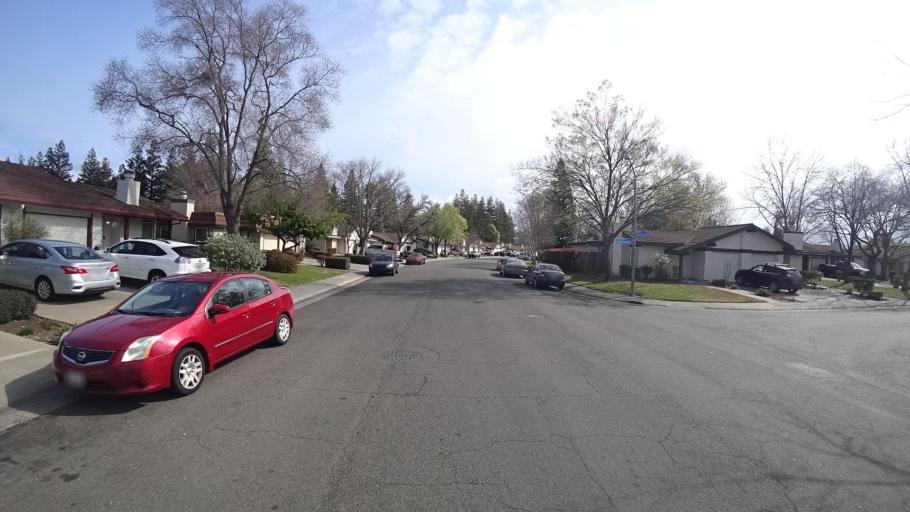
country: US
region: California
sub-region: Sacramento County
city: Gold River
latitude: 38.6128
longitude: -121.2745
